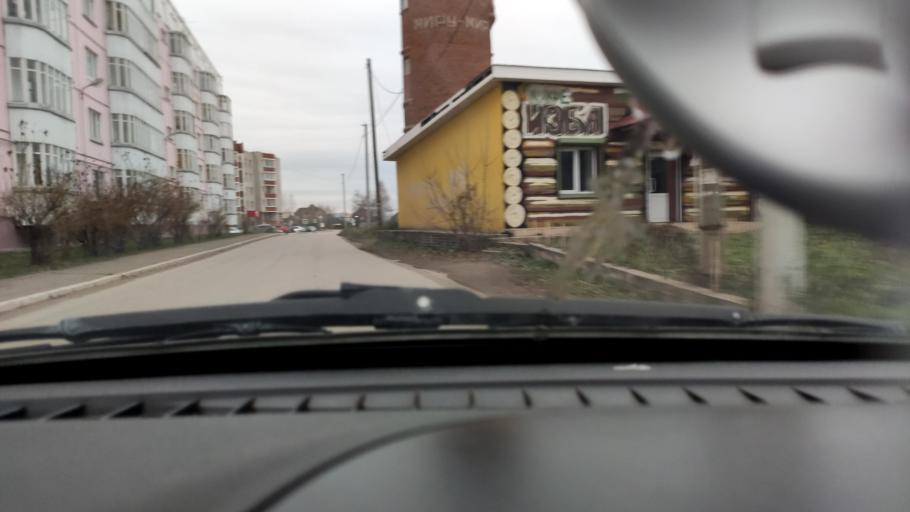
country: RU
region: Perm
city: Kondratovo
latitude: 57.9797
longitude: 56.1064
